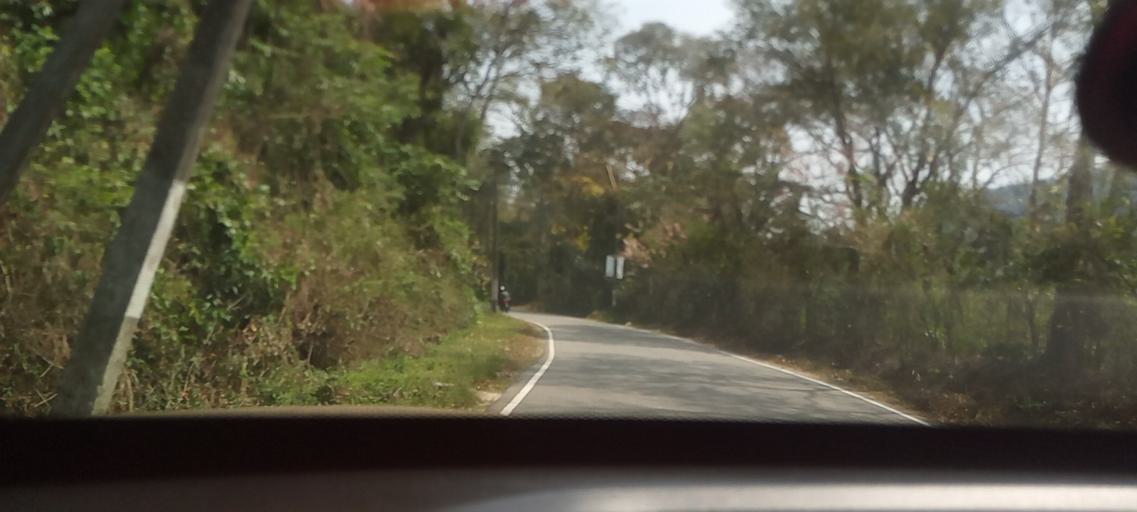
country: IN
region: Karnataka
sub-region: Chikmagalur
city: Mudigere
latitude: 13.2771
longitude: 75.6078
